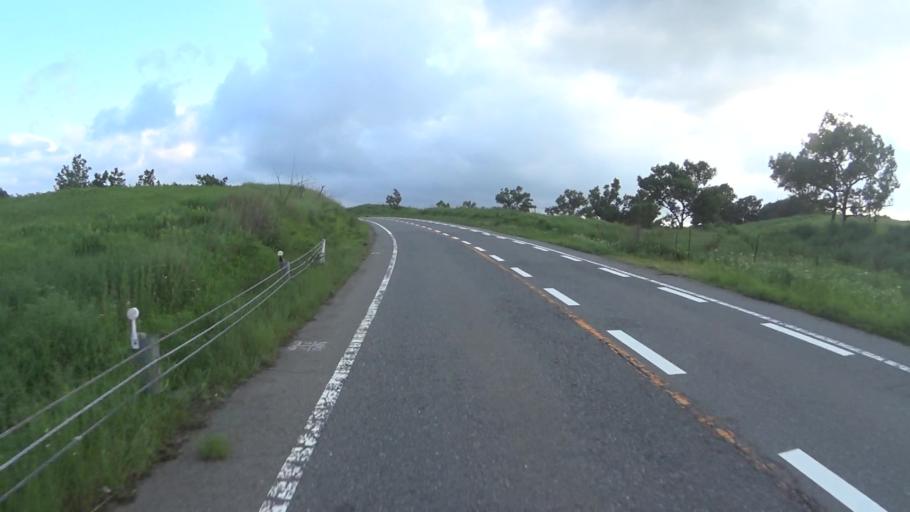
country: JP
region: Kumamoto
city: Aso
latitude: 33.0082
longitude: 131.0255
